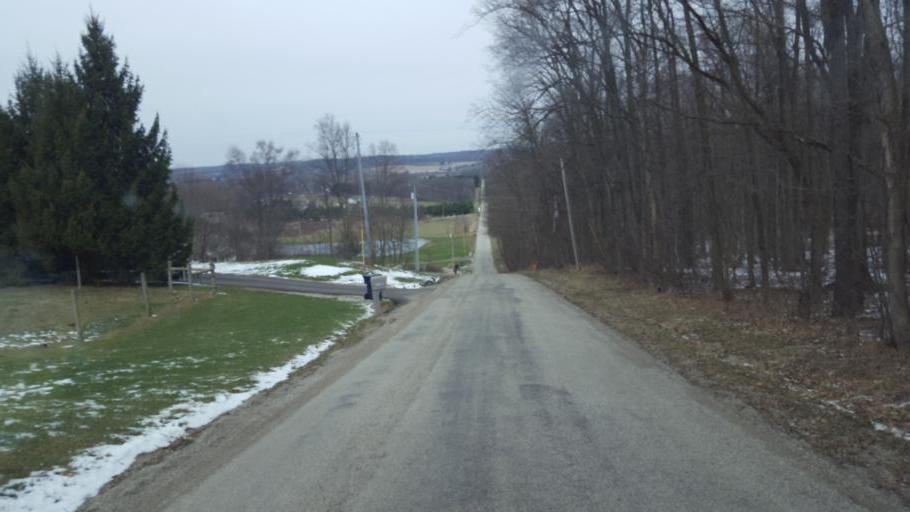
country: US
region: Ohio
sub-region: Sandusky County
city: Bellville
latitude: 40.5946
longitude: -82.5677
